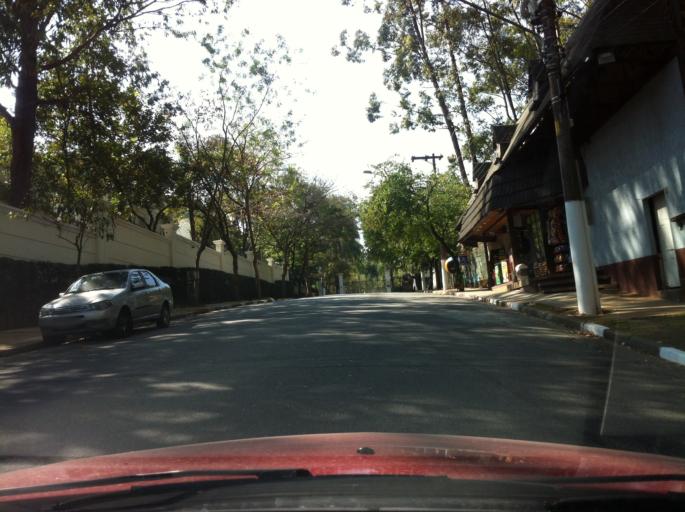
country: BR
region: Sao Paulo
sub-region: Diadema
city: Diadema
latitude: -23.6490
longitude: -46.6939
